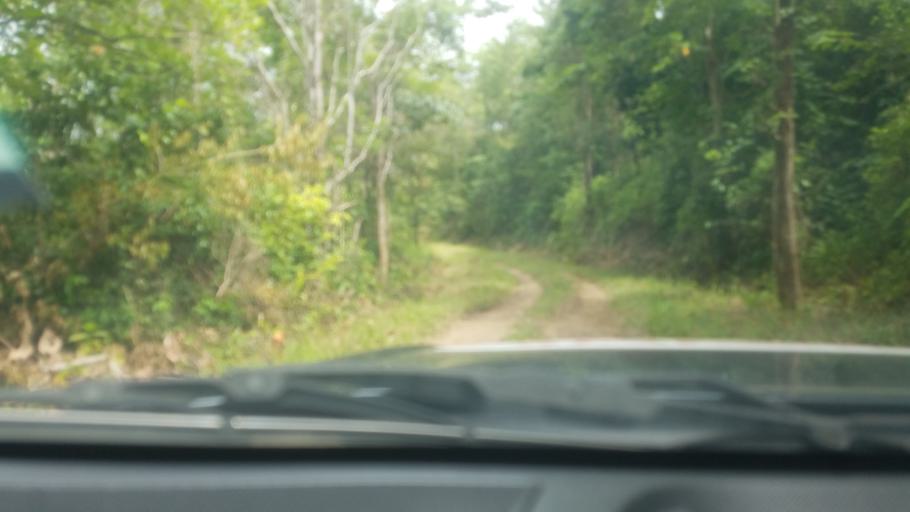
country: LC
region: Micoud Quarter
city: Micoud
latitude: 13.8057
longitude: -60.9314
